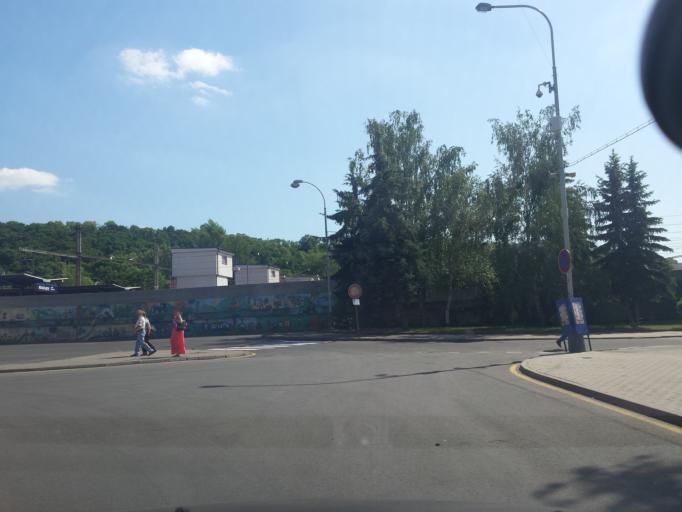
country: CZ
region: Central Bohemia
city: Kralupy nad Vltavou
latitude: 50.2395
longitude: 14.3125
